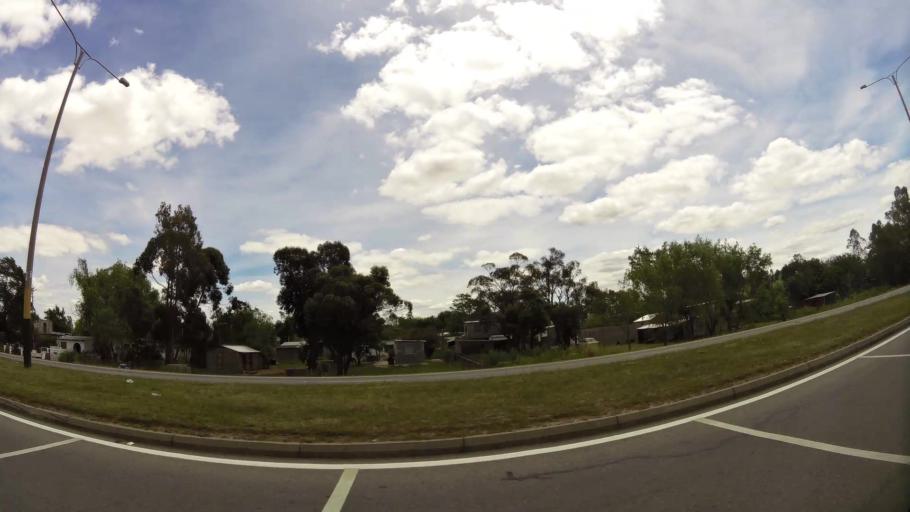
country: UY
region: Canelones
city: Pando
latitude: -34.8034
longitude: -55.9542
